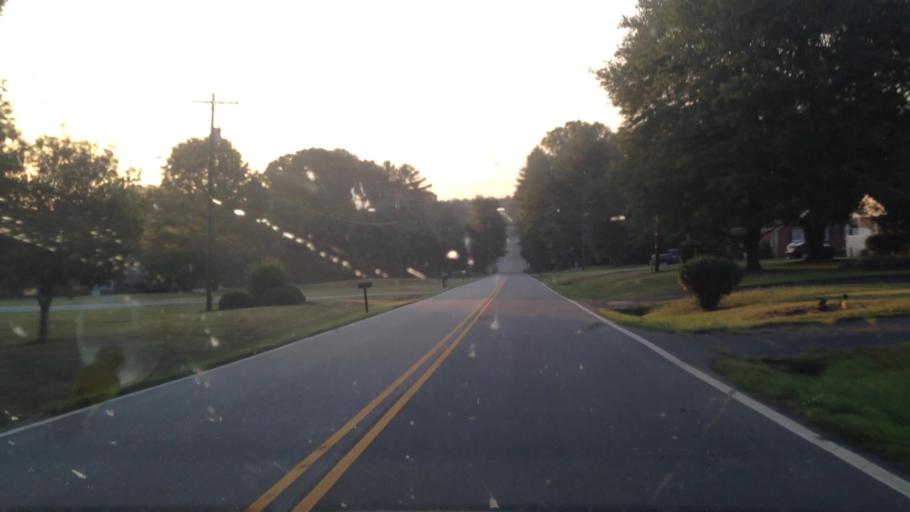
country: US
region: North Carolina
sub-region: Forsyth County
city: Kernersville
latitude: 36.1566
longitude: -80.1044
